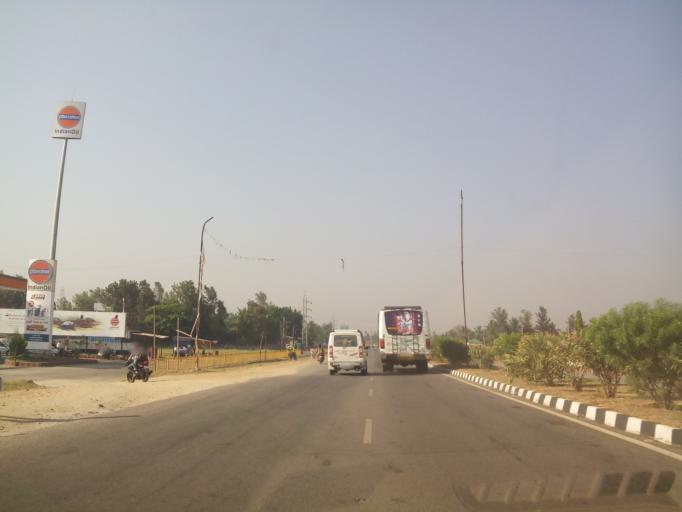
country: IN
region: Karnataka
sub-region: Bangalore Rural
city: Nelamangala
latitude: 13.0894
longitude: 77.3763
